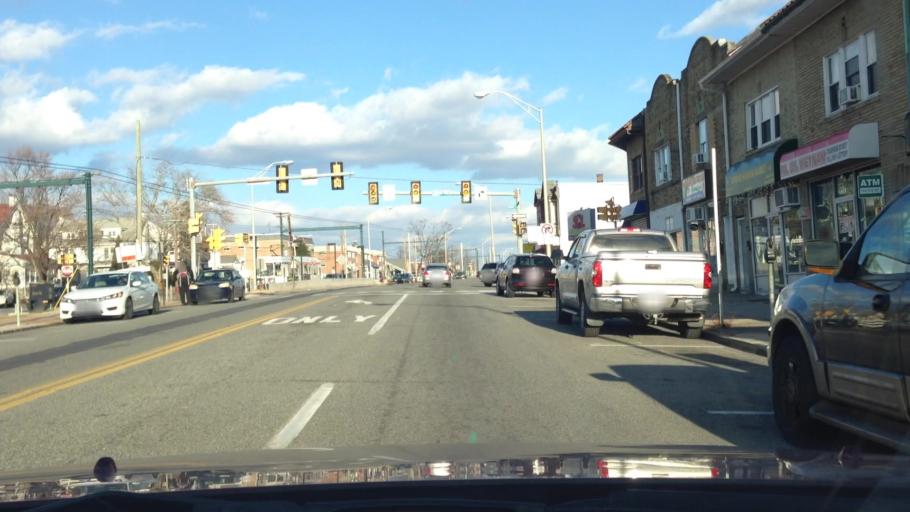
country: US
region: Pennsylvania
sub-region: Delaware County
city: East Lansdowne
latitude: 39.9572
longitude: -75.2695
